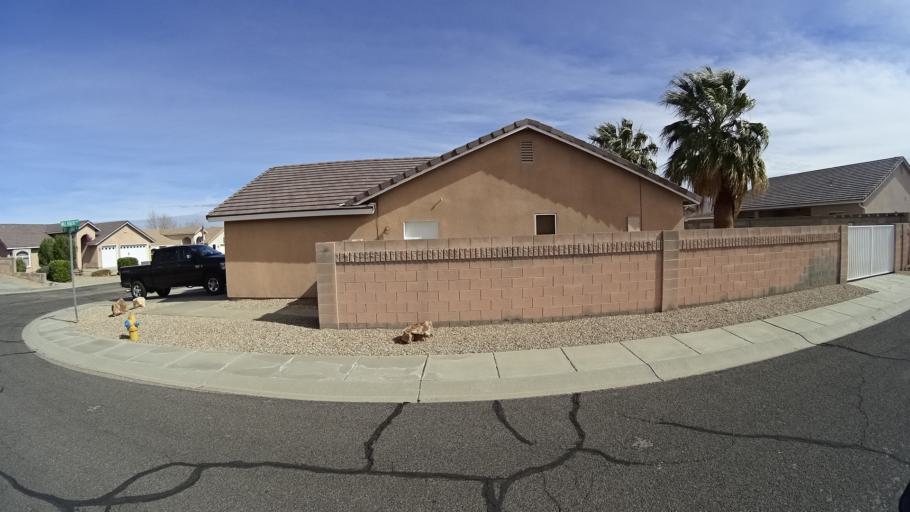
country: US
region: Arizona
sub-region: Mohave County
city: New Kingman-Butler
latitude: 35.2351
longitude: -114.0331
